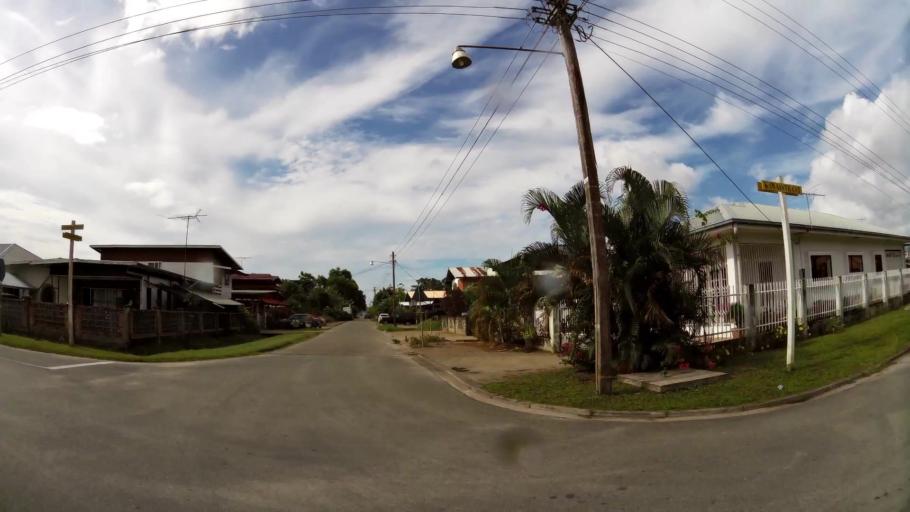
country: SR
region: Paramaribo
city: Paramaribo
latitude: 5.8455
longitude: -55.2056
